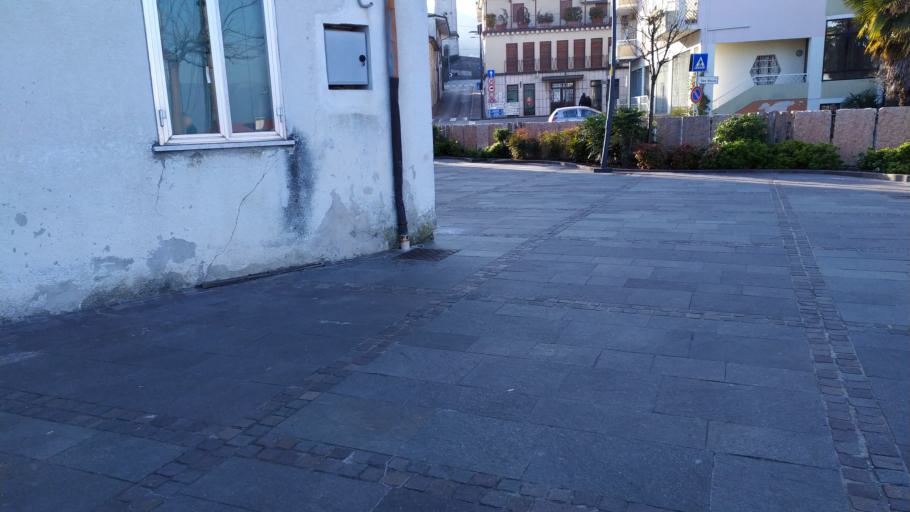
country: IT
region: Veneto
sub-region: Provincia di Vicenza
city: Monte di Malo
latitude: 45.6605
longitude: 11.3632
